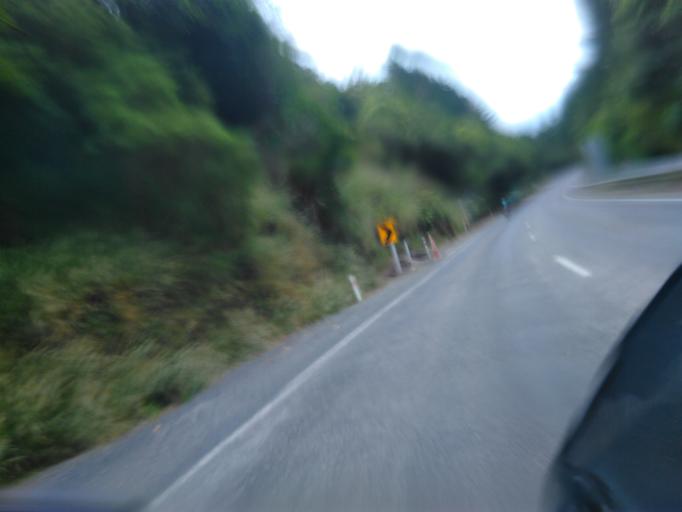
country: NZ
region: Bay of Plenty
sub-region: Opotiki District
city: Opotiki
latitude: -38.3451
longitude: 177.4522
